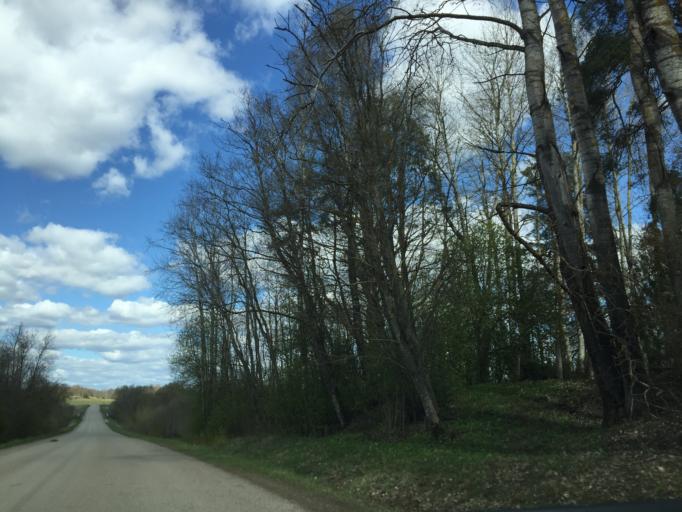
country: LV
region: Rezekne
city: Rezekne
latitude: 56.5465
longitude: 27.1498
